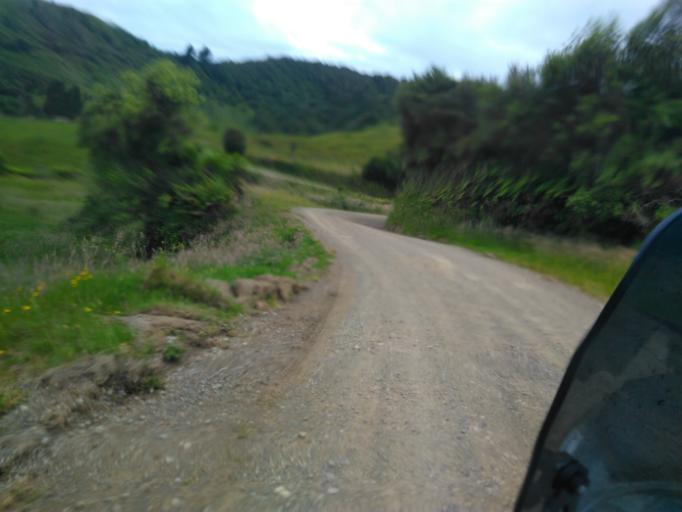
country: NZ
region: Bay of Plenty
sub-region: Opotiki District
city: Opotiki
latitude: -38.1035
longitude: 177.4967
